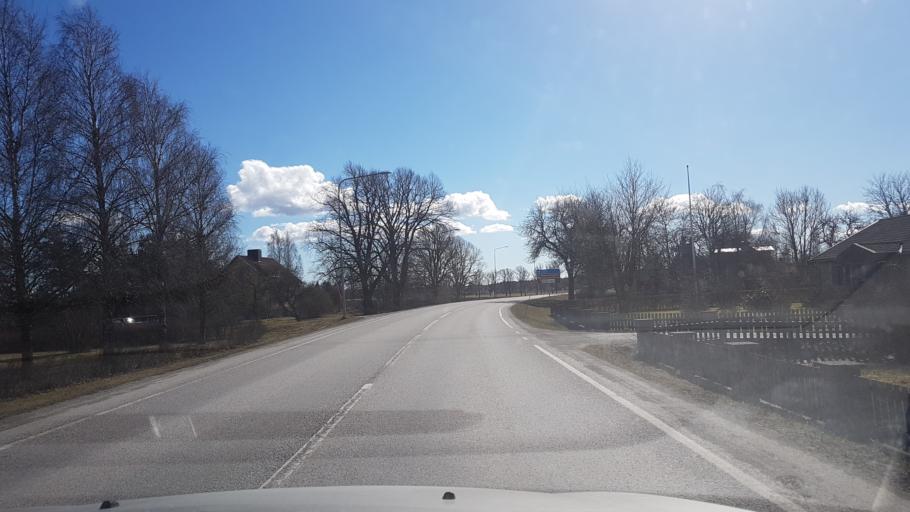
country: SE
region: Gotland
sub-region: Gotland
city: Visby
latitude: 57.5175
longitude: 18.4439
